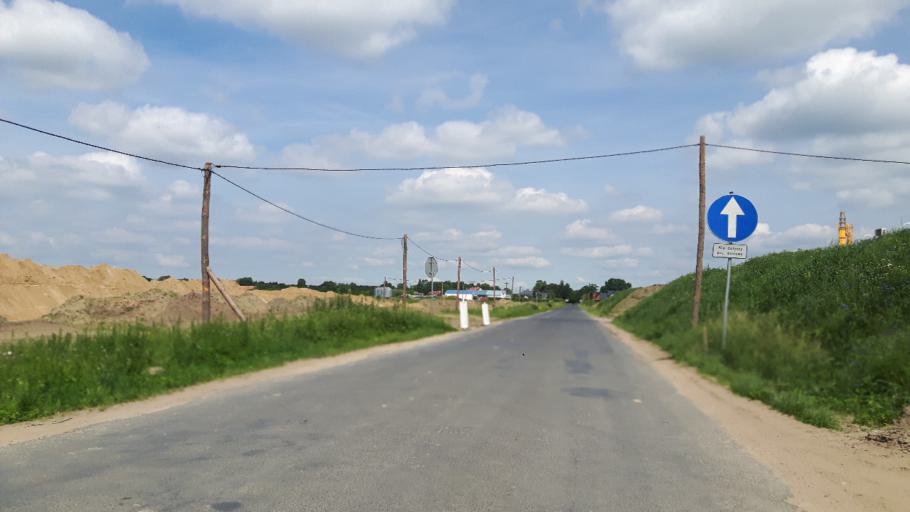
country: PL
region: West Pomeranian Voivodeship
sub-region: Powiat goleniowski
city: Goleniow
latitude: 53.5906
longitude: 14.8660
